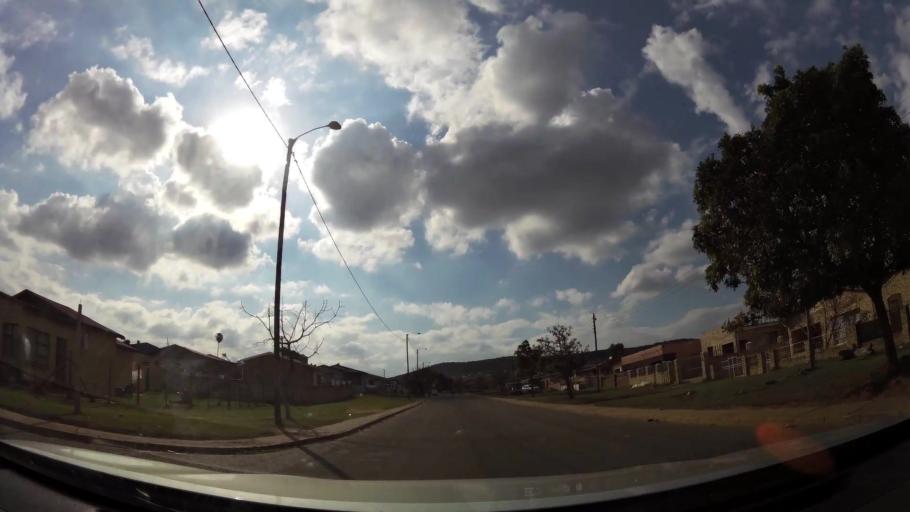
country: ZA
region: Eastern Cape
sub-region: Nelson Mandela Bay Metropolitan Municipality
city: Uitenhage
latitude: -33.7377
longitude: 25.3813
